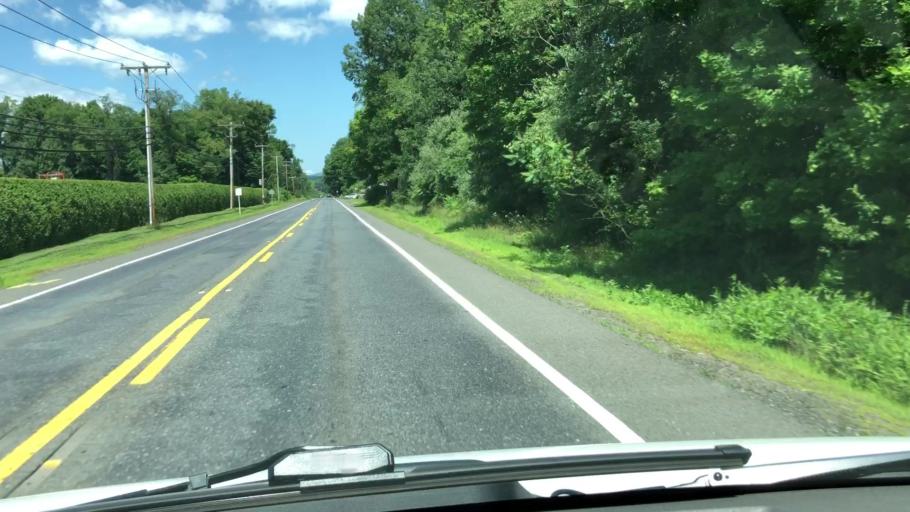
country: US
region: Massachusetts
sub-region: Franklin County
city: Greenfield
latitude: 42.5445
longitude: -72.6015
